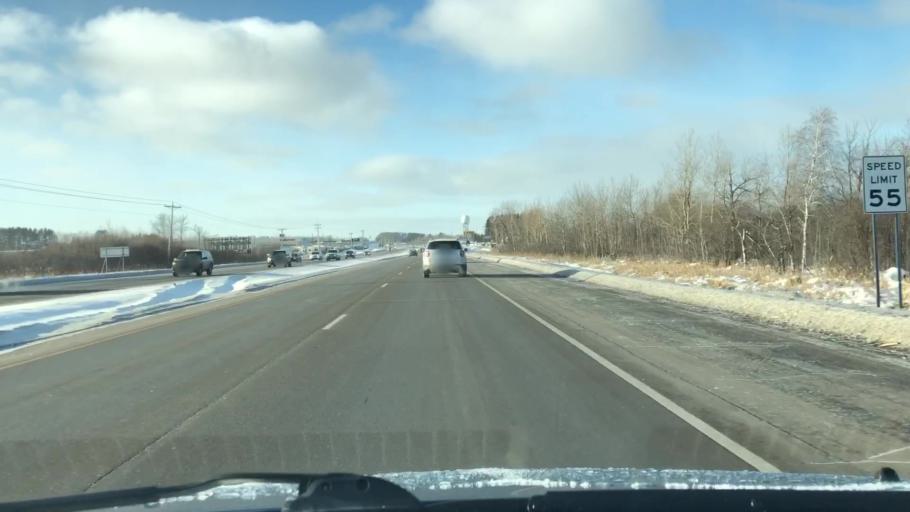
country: US
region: Minnesota
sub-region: Saint Louis County
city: Hermantown
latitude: 46.8298
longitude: -92.1991
